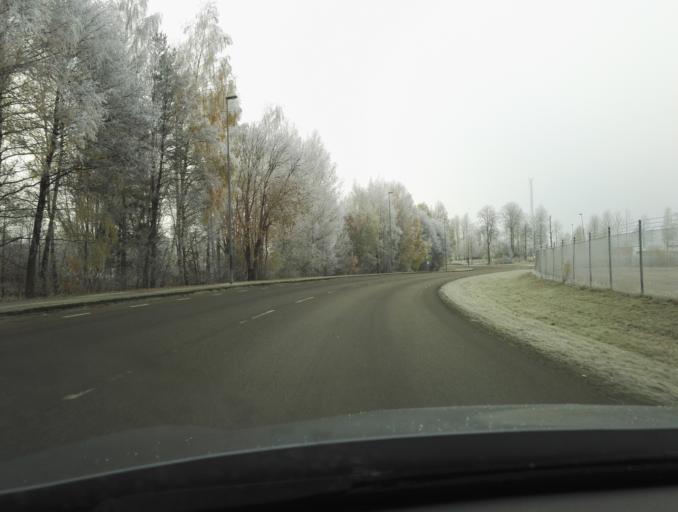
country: SE
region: Kronoberg
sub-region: Vaxjo Kommun
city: Vaexjoe
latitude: 56.8852
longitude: 14.7356
